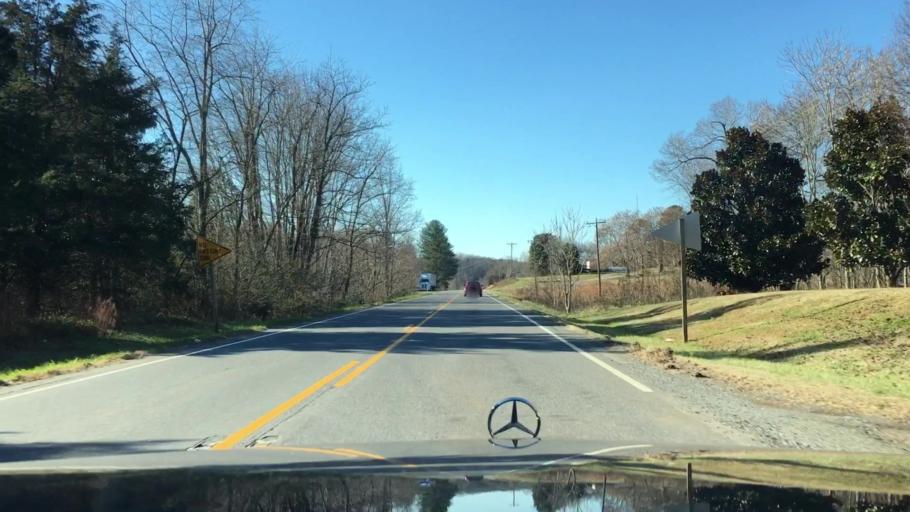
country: US
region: Virginia
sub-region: City of Bedford
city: Bedford
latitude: 37.2402
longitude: -79.5951
